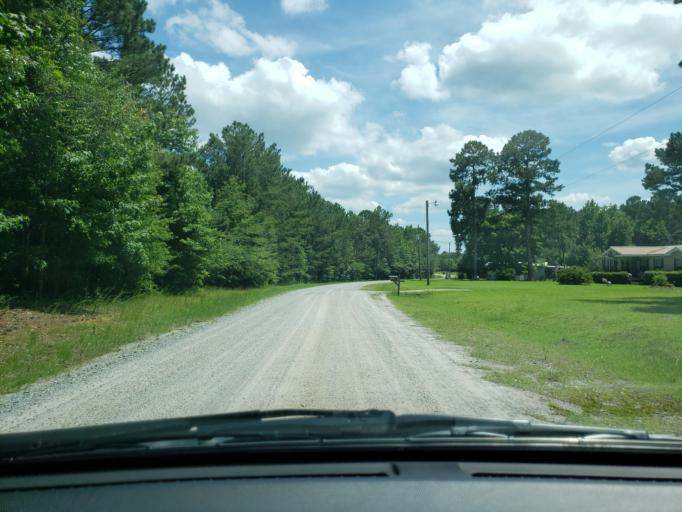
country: US
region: Alabama
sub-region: Elmore County
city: Eclectic
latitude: 32.6265
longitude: -85.9452
